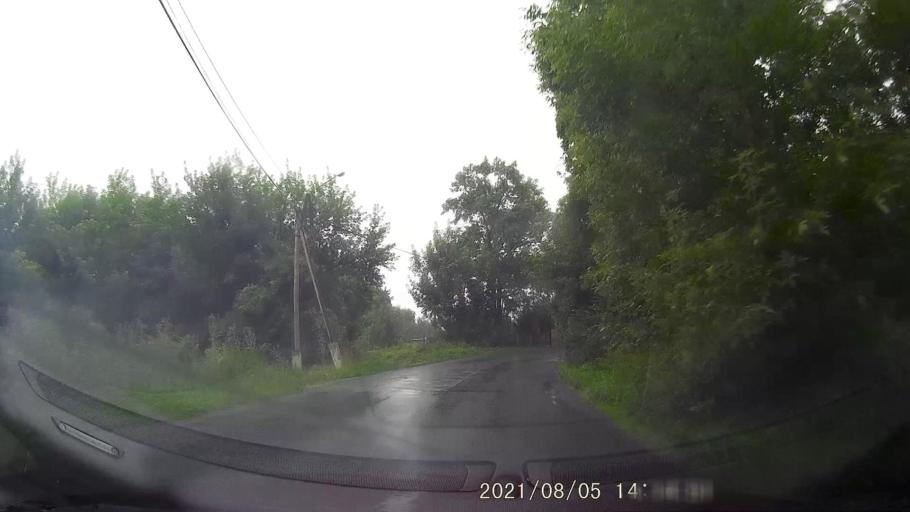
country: PL
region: Opole Voivodeship
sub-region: Powiat prudnicki
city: Biala
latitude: 50.4661
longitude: 17.7380
